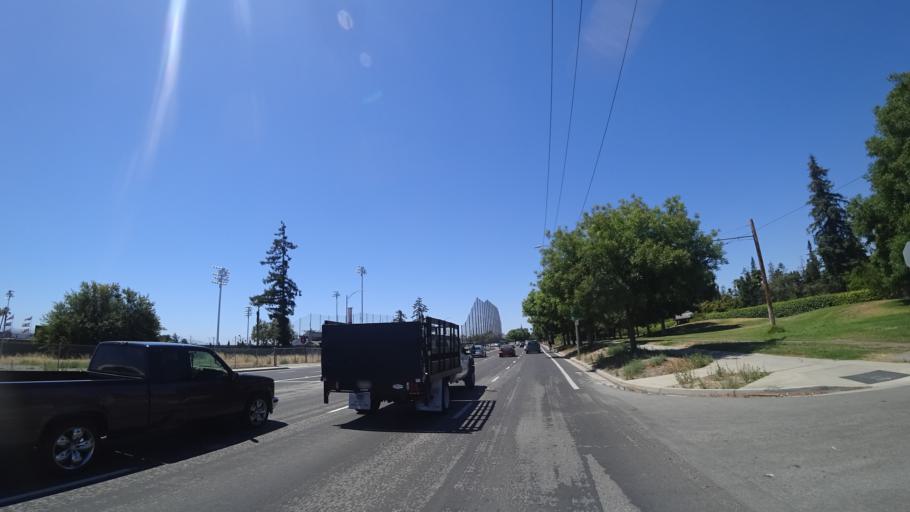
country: US
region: California
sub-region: Santa Clara County
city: San Jose
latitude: 37.3204
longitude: -121.8604
